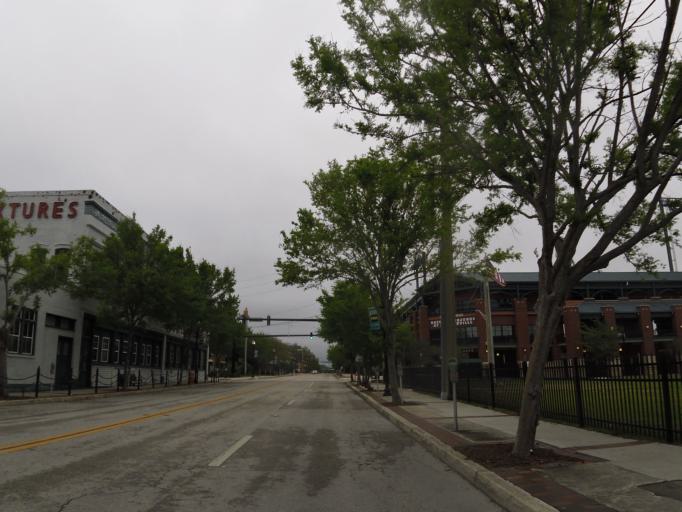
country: US
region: Florida
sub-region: Duval County
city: Jacksonville
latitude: 30.3239
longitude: -81.6443
